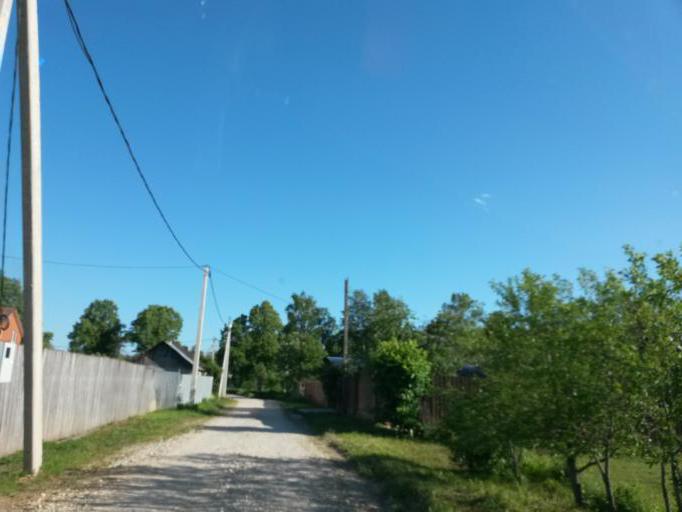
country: RU
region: Moskovskaya
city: Lyubuchany
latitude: 55.2523
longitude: 37.6080
